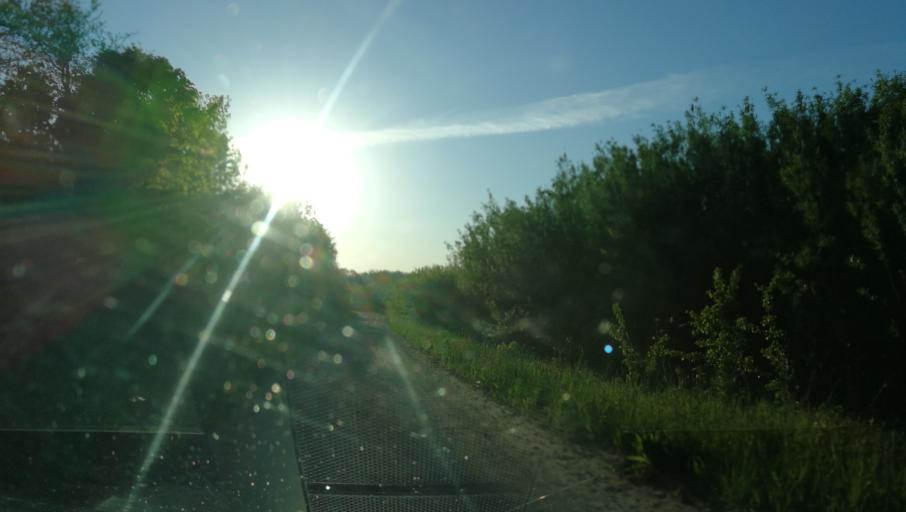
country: LV
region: Dobeles Rajons
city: Dobele
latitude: 56.6193
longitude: 23.2992
